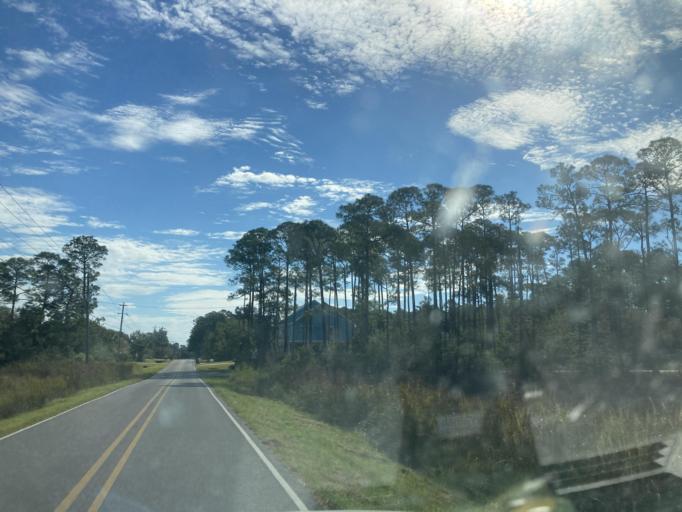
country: US
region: Mississippi
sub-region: Jackson County
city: Saint Martin
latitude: 30.4358
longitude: -88.8633
